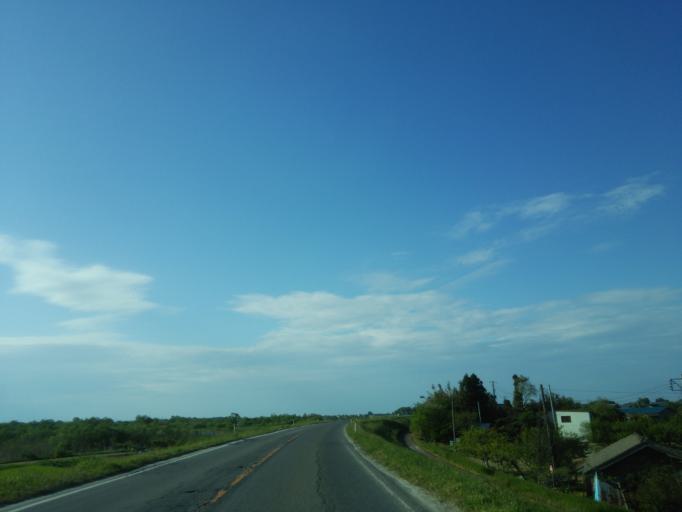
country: JP
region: Niigata
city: Gosen
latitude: 37.7887
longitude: 139.1840
